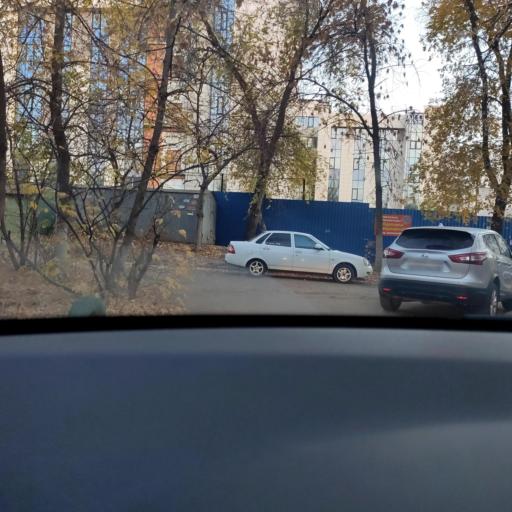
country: RU
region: Samara
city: Samara
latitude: 53.1889
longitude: 50.1870
